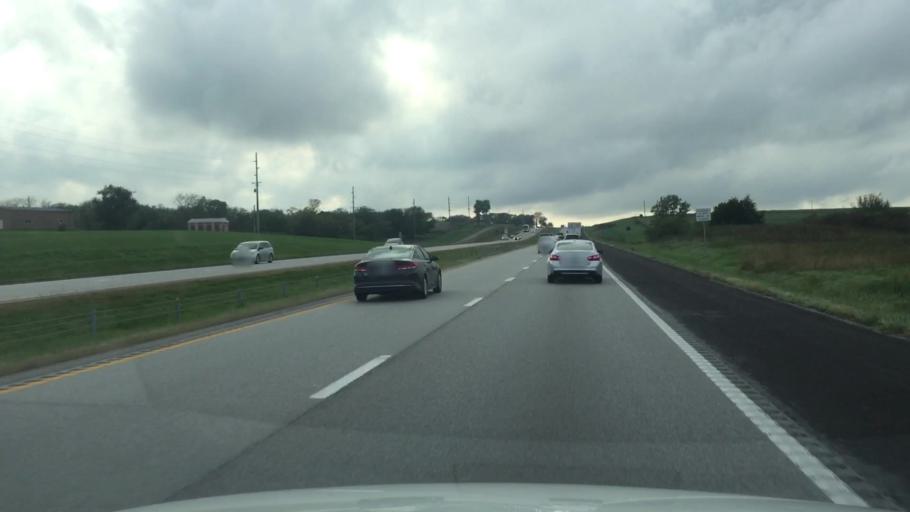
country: US
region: Missouri
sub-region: Lafayette County
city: Concordia
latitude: 38.9925
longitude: -93.6071
